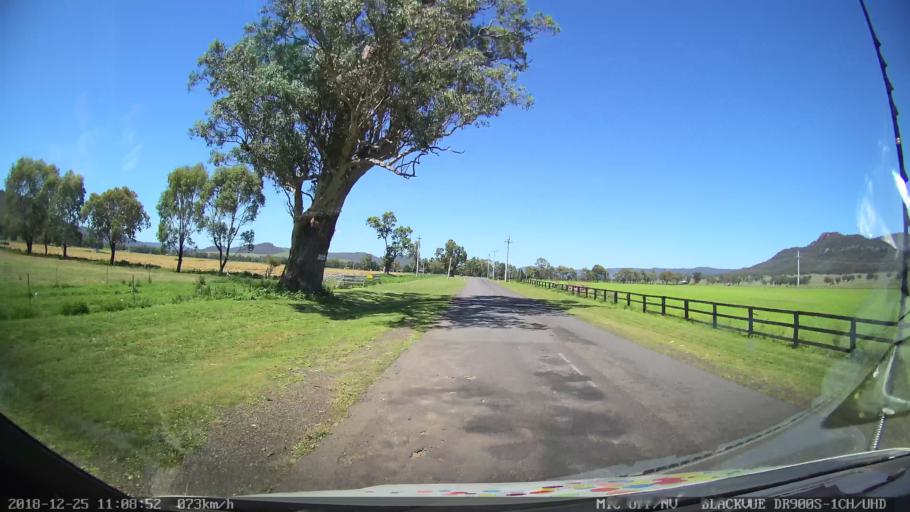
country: AU
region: New South Wales
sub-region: Upper Hunter Shire
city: Merriwa
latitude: -32.4057
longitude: 150.1214
